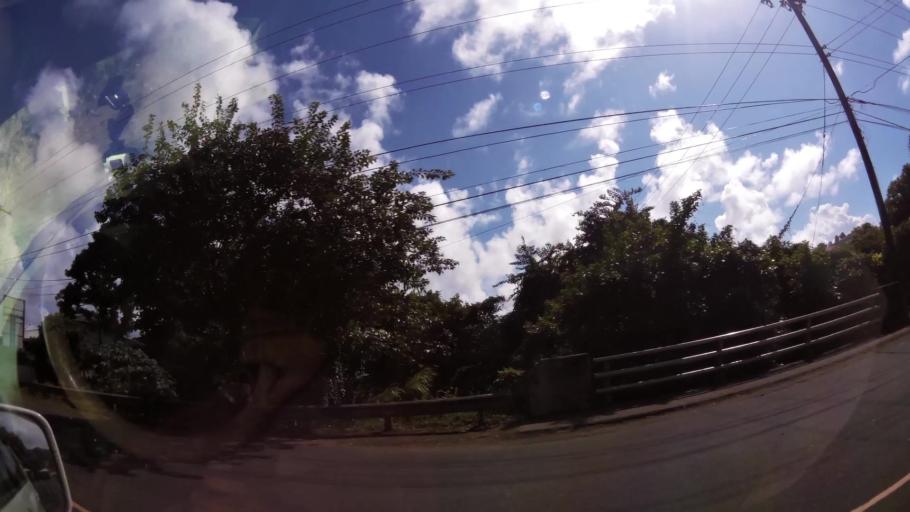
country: VC
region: Saint George
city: Kingstown
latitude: 13.1438
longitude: -61.1719
